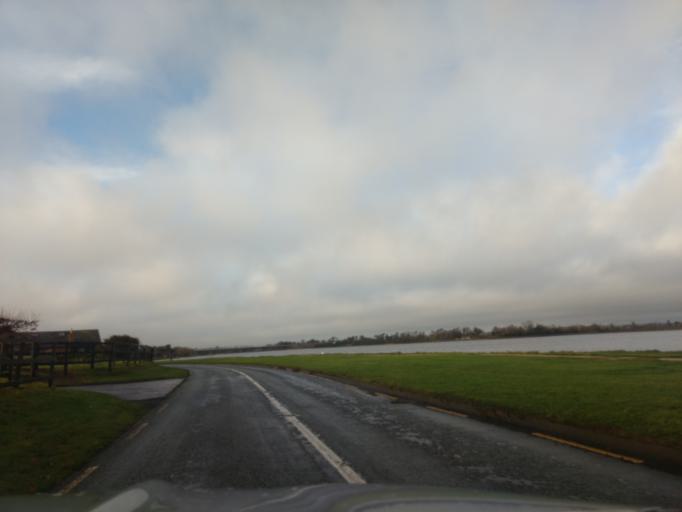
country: IE
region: Leinster
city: Kinsealy-Drinan
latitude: 53.4594
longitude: -6.1843
